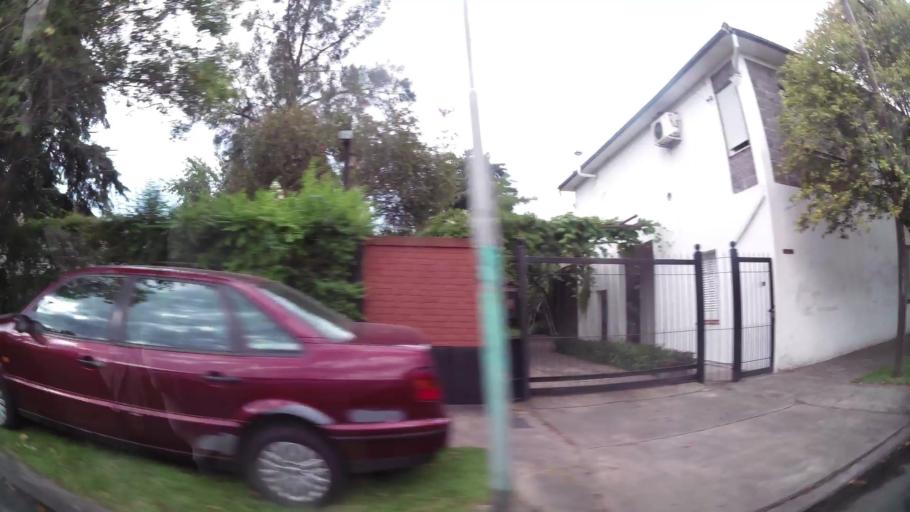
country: AR
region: Buenos Aires
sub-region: Partido de Tigre
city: Tigre
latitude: -34.4688
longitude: -58.6535
